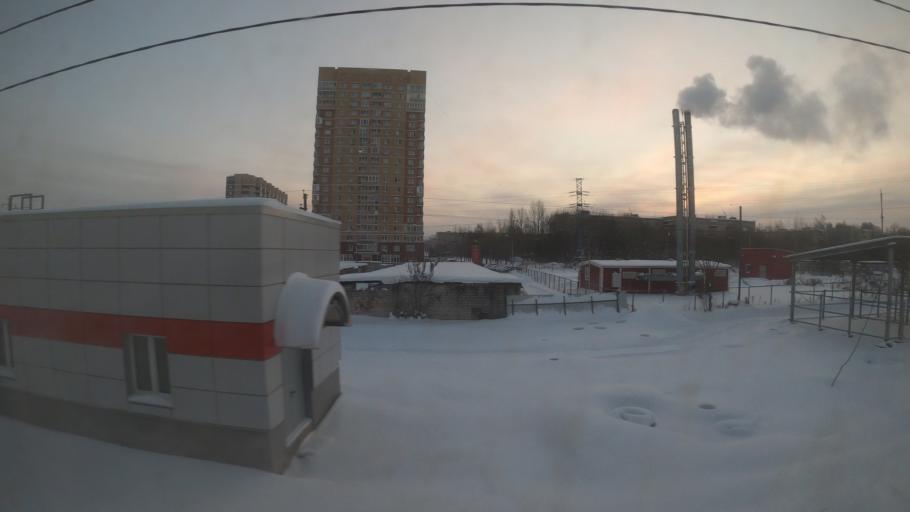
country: RU
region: Moskovskaya
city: Lobnya
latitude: 56.0249
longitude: 37.4859
